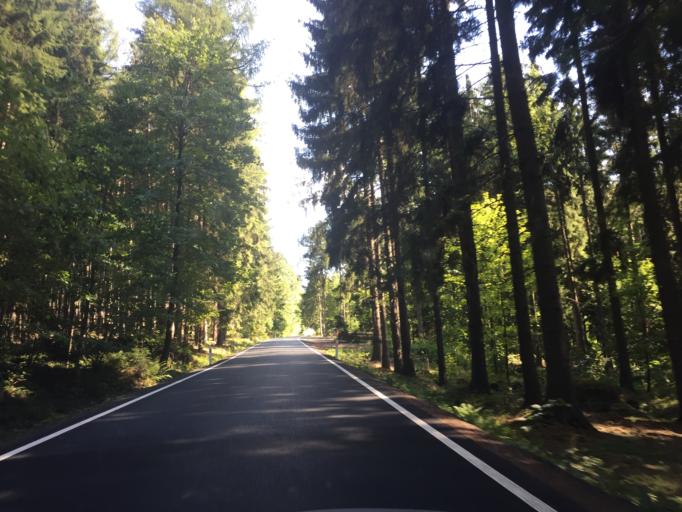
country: CZ
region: Liberecky
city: Mala Skala
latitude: 50.6360
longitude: 15.2102
